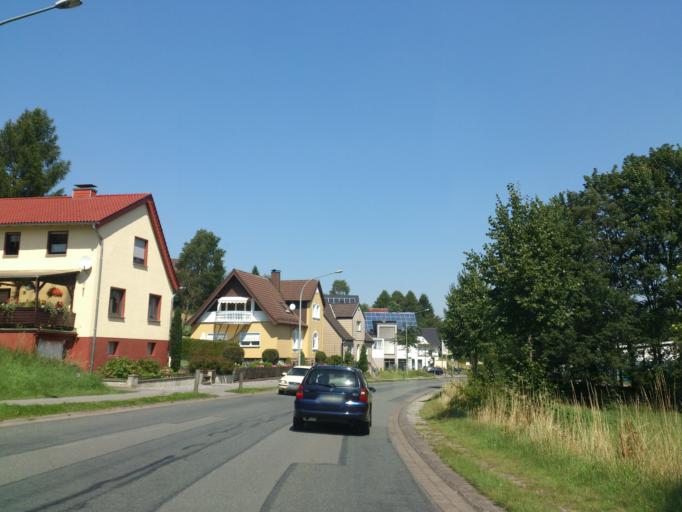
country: DE
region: North Rhine-Westphalia
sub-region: Regierungsbezirk Detmold
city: Altenbeken
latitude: 51.7535
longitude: 8.9514
